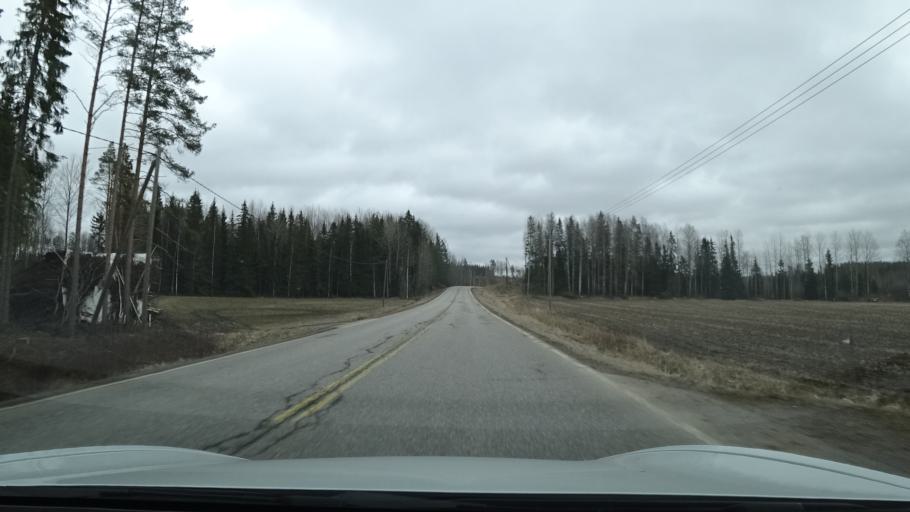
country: FI
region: Uusimaa
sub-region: Porvoo
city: Myrskylae
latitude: 60.6603
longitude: 25.7411
